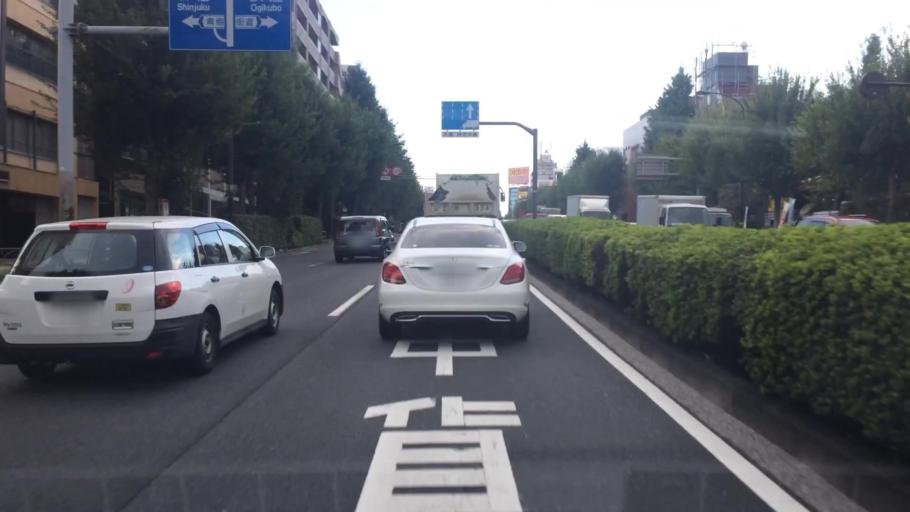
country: JP
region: Tokyo
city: Tokyo
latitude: 35.7011
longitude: 139.6548
